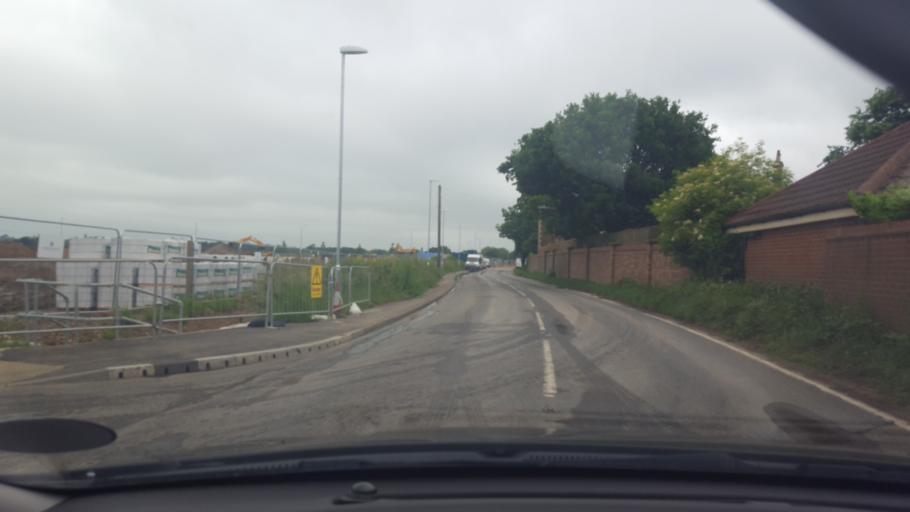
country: GB
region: England
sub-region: Essex
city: Great Horkesley
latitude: 51.9176
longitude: 0.8902
